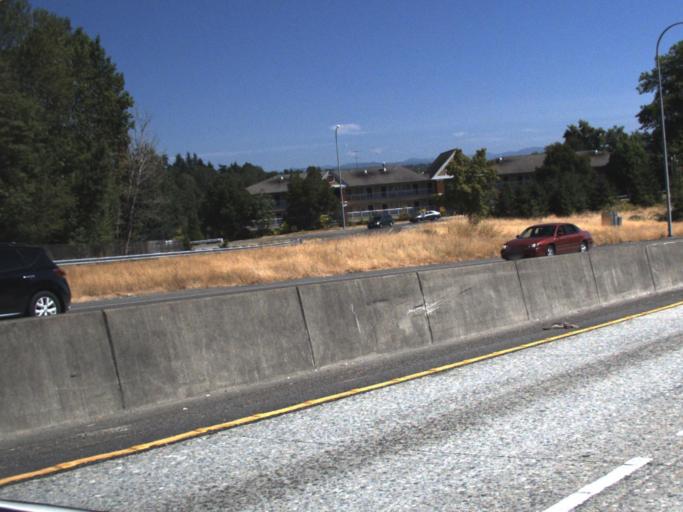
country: US
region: Washington
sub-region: King County
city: Tukwila
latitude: 47.4644
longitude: -122.2725
